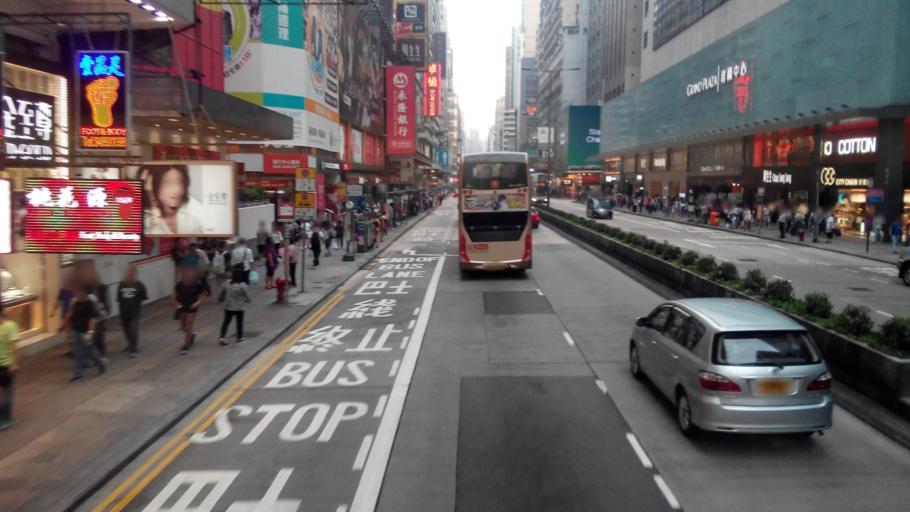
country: HK
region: Kowloon City
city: Kowloon
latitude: 22.3186
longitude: 114.1695
